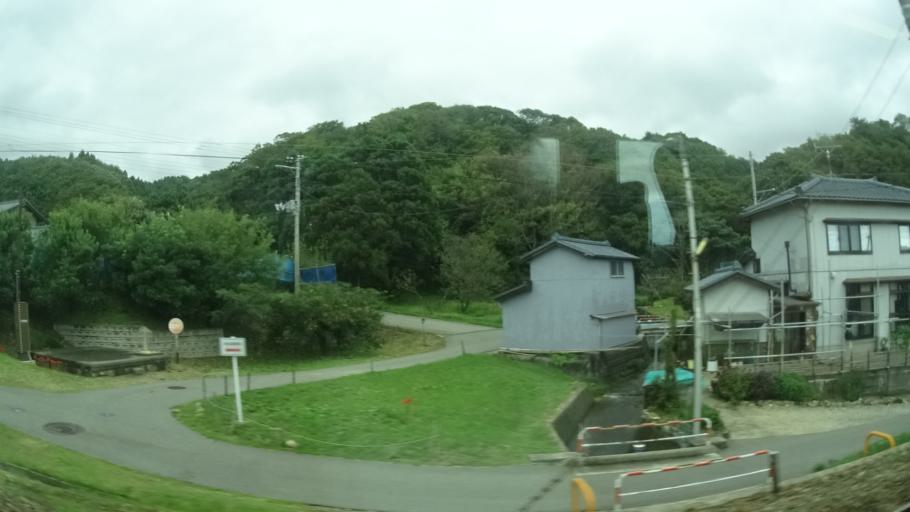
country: JP
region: Niigata
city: Murakami
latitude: 38.2760
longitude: 139.4508
